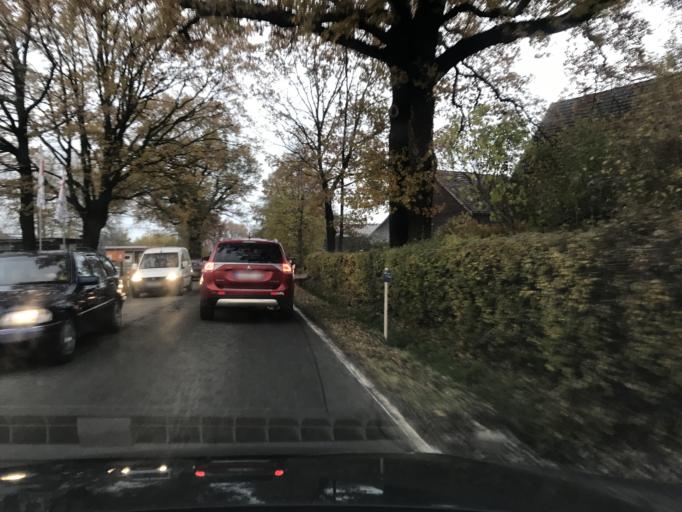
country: DE
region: North Rhine-Westphalia
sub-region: Regierungsbezirk Arnsberg
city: Welver
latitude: 51.6663
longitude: 7.9829
